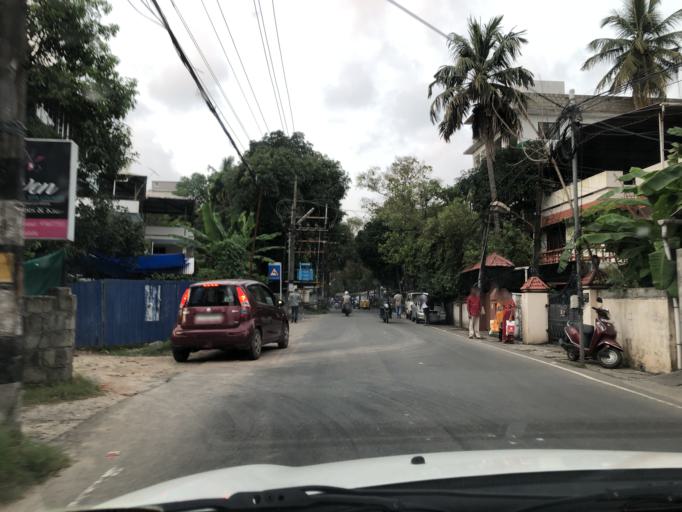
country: IN
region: Kerala
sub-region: Ernakulam
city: Cochin
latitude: 9.9609
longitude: 76.3012
